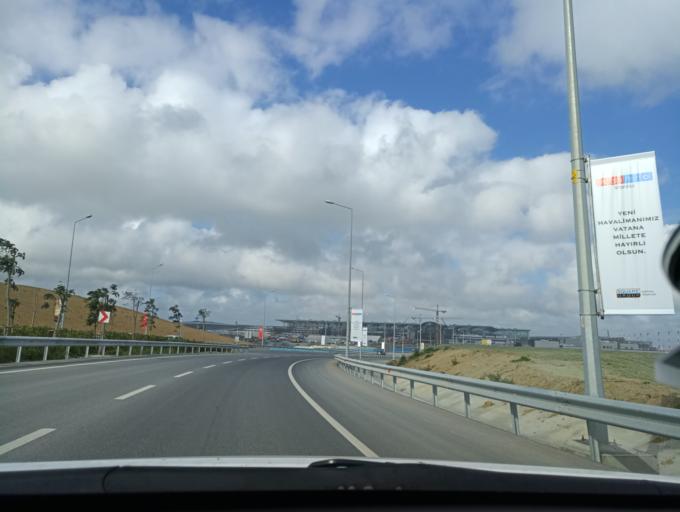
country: TR
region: Istanbul
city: Durusu
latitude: 41.2469
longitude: 28.7471
